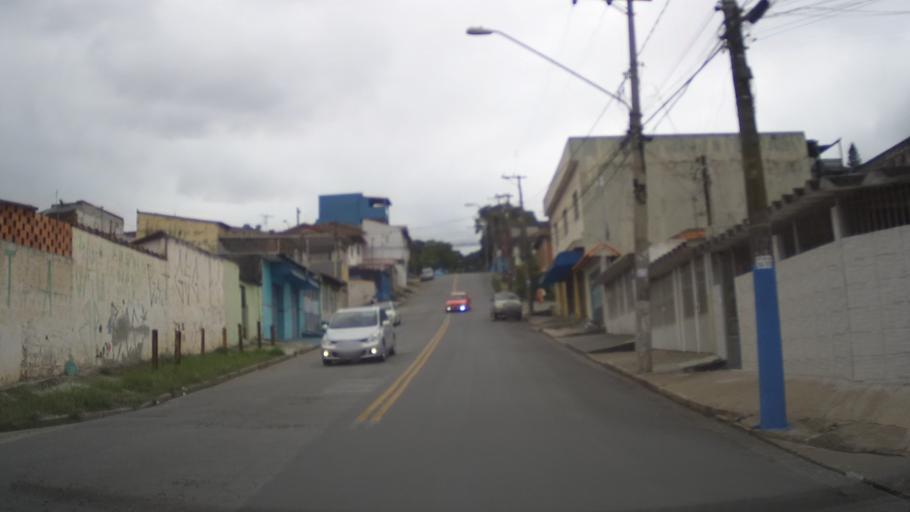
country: BR
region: Sao Paulo
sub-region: Guarulhos
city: Guarulhos
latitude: -23.4430
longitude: -46.5112
